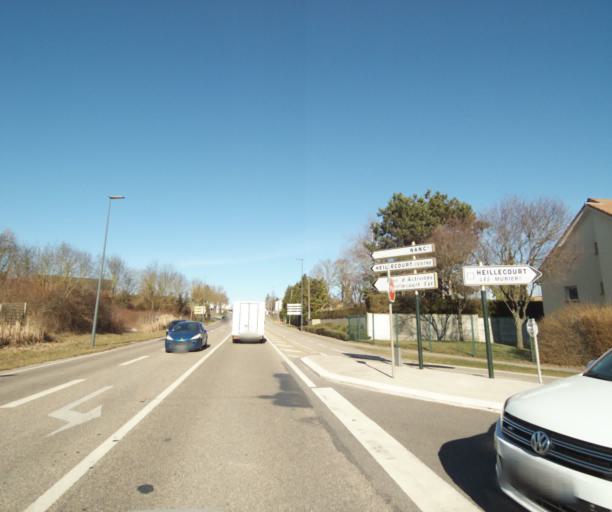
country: FR
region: Lorraine
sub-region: Departement de Meurthe-et-Moselle
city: Vandoeuvre-les-Nancy
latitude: 48.6505
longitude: 6.1838
